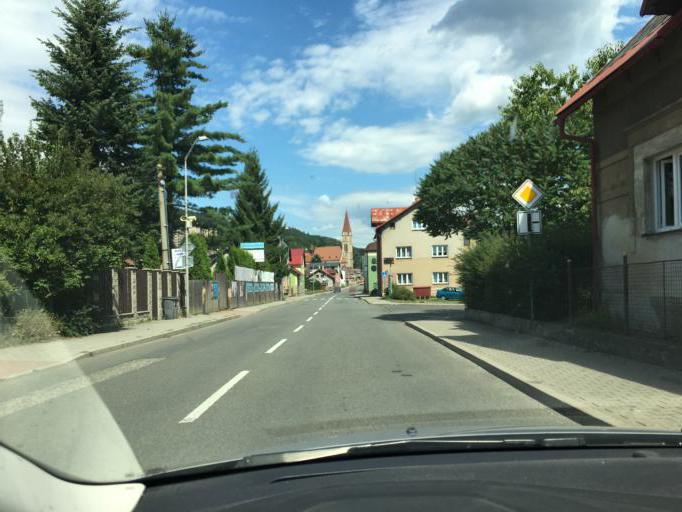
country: CZ
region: Liberecky
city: Velke Hamry
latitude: 50.7137
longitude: 15.3156
